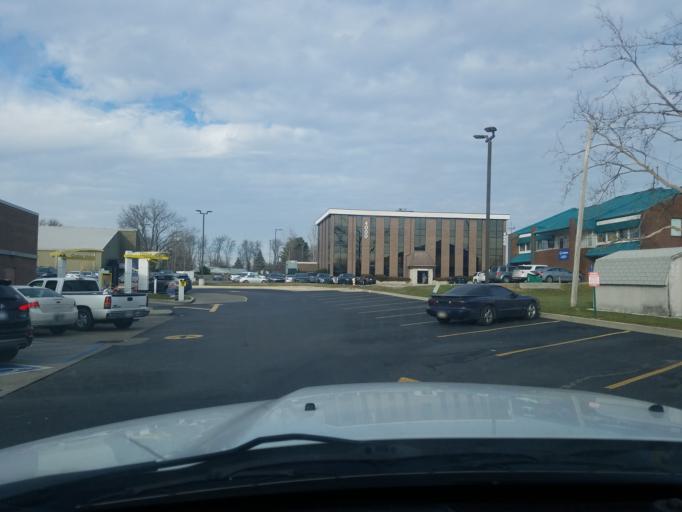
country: US
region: Indiana
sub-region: Marion County
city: Southport
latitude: 39.6658
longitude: -86.0978
